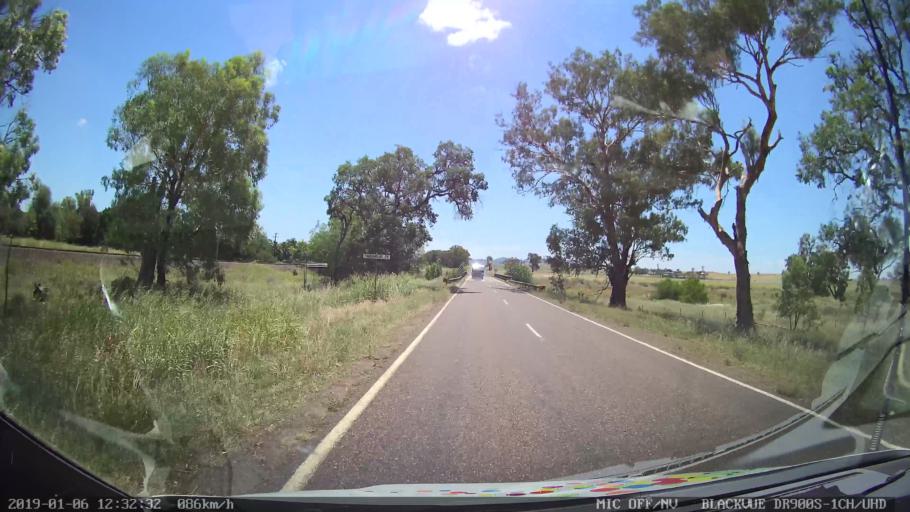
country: AU
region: New South Wales
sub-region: Tamworth Municipality
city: Phillip
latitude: -31.1517
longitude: 150.8721
